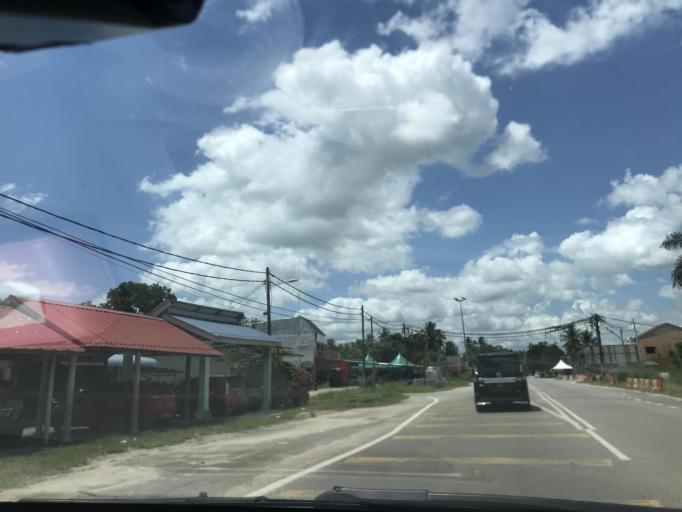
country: TH
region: Narathiwat
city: Tak Bai
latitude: 6.2276
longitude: 102.0959
